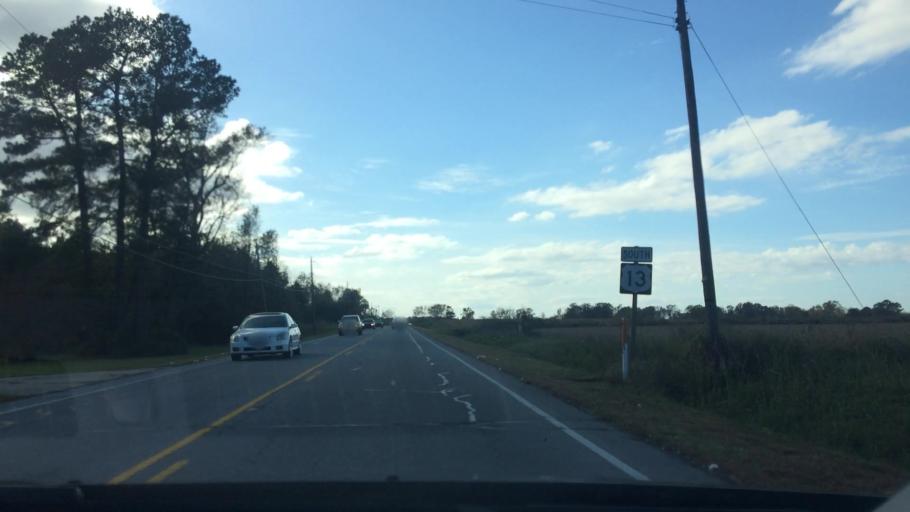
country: US
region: North Carolina
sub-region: Greene County
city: Snow Hill
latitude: 35.4380
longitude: -77.7608
